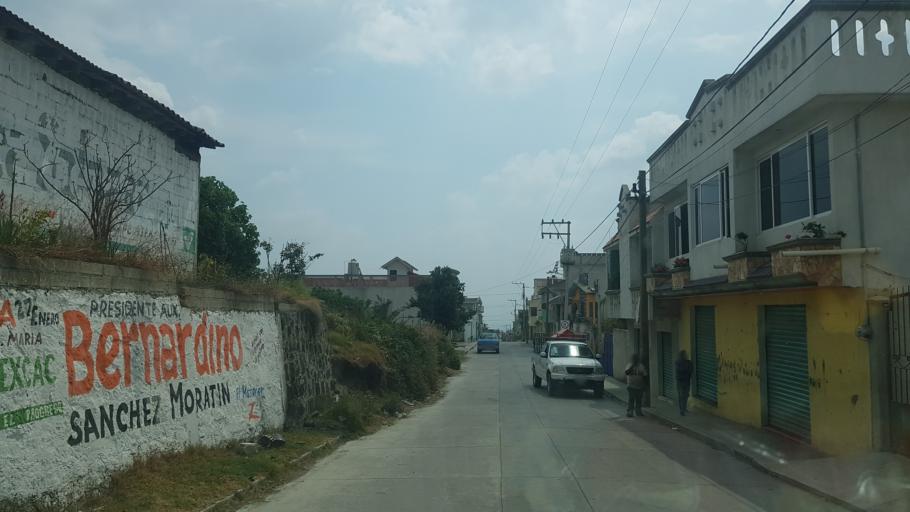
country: MX
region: Puebla
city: Domingo Arenas
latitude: 19.1358
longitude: -98.4918
